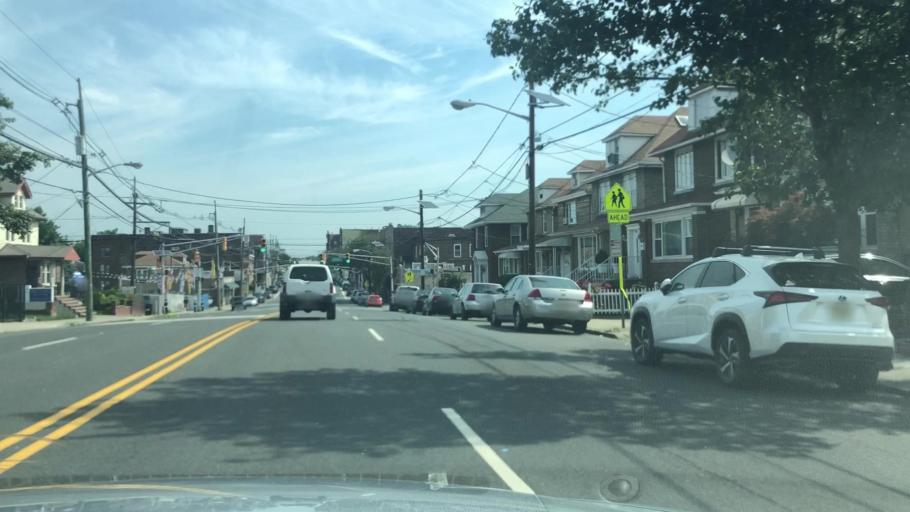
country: US
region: New Jersey
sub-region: Hudson County
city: North Bergen
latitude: 40.8050
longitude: -74.0105
